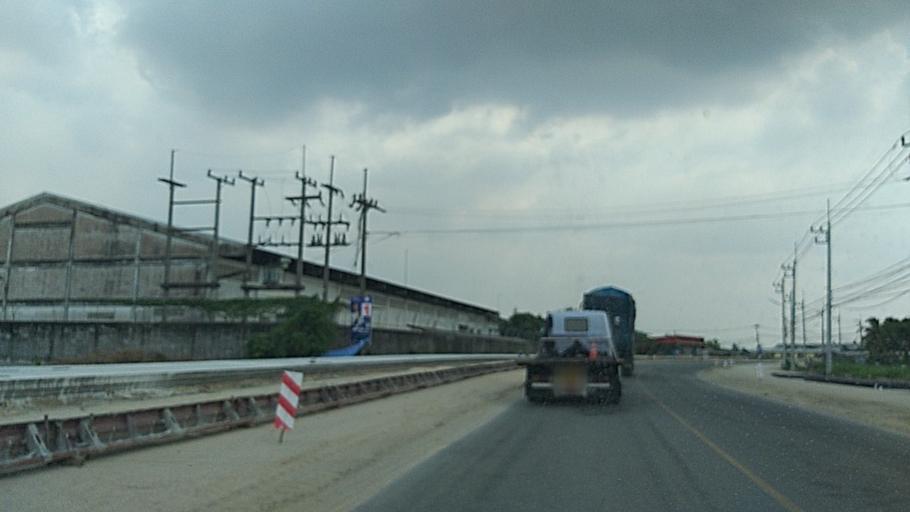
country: TH
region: Chon Buri
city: Ban Bueng
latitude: 13.3137
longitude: 101.1840
